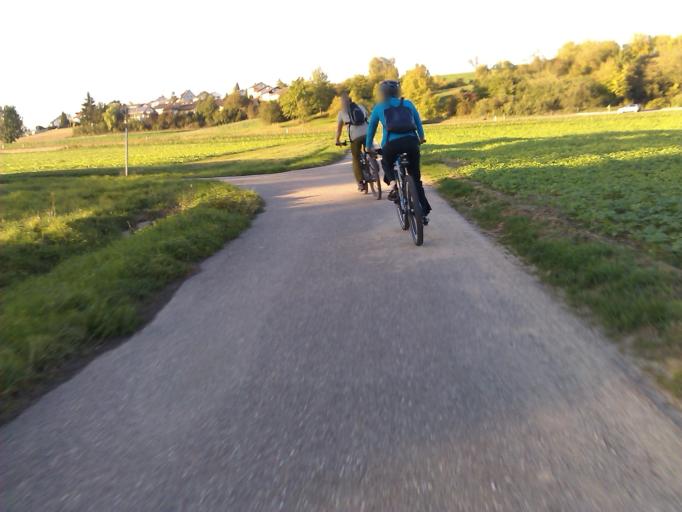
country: DE
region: Baden-Wuerttemberg
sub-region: Regierungsbezirk Stuttgart
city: Ittlingen
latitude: 49.1815
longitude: 8.9383
